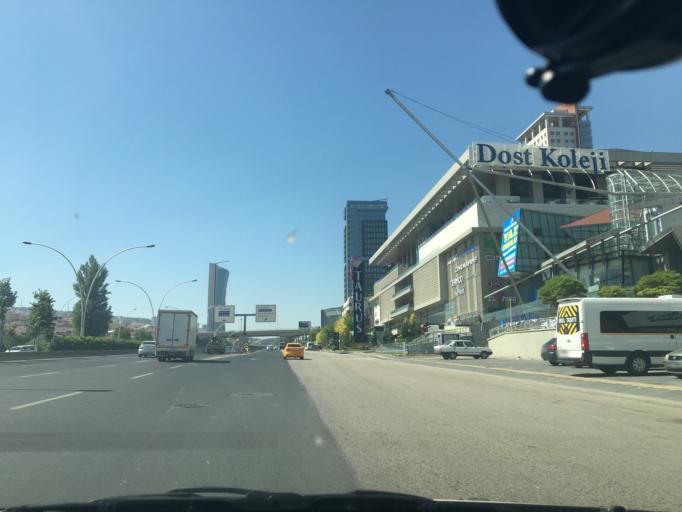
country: TR
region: Ankara
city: Ankara
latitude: 39.8900
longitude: 32.8125
